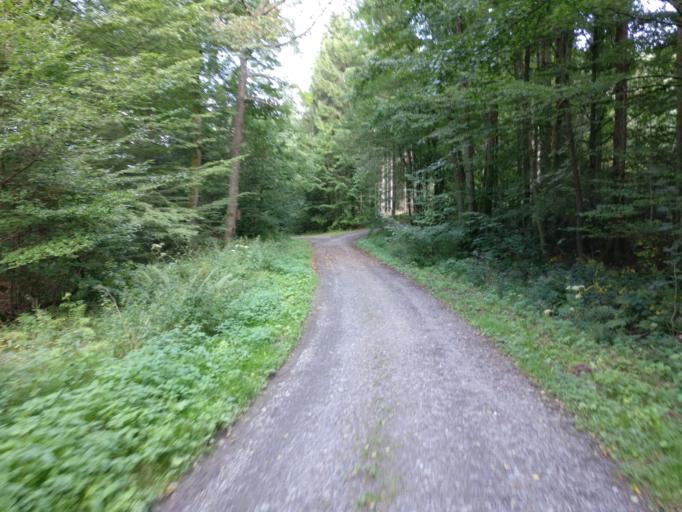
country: DE
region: Hesse
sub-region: Regierungsbezirk Giessen
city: Greifenstein
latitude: 50.6286
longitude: 8.2780
